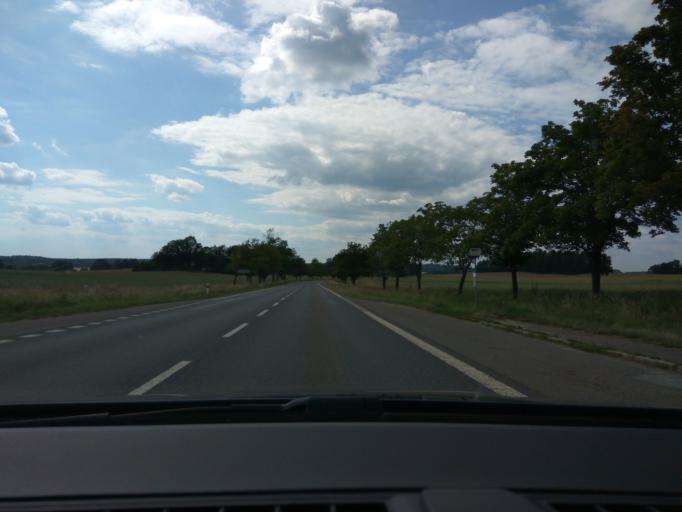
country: CZ
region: Jihocesky
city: Milevsko
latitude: 49.4686
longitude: 14.3069
